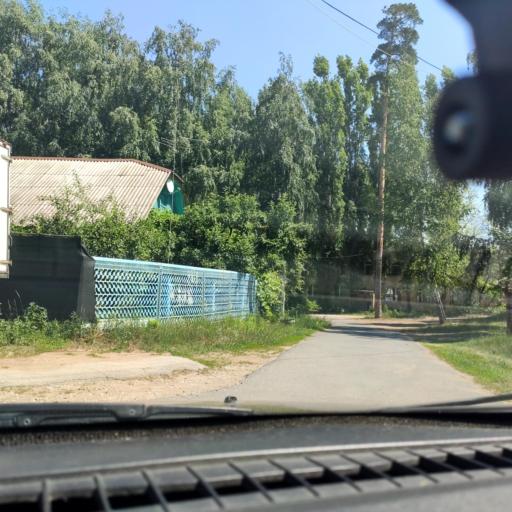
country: RU
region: Samara
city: Tol'yatti
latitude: 53.5011
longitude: 49.3551
